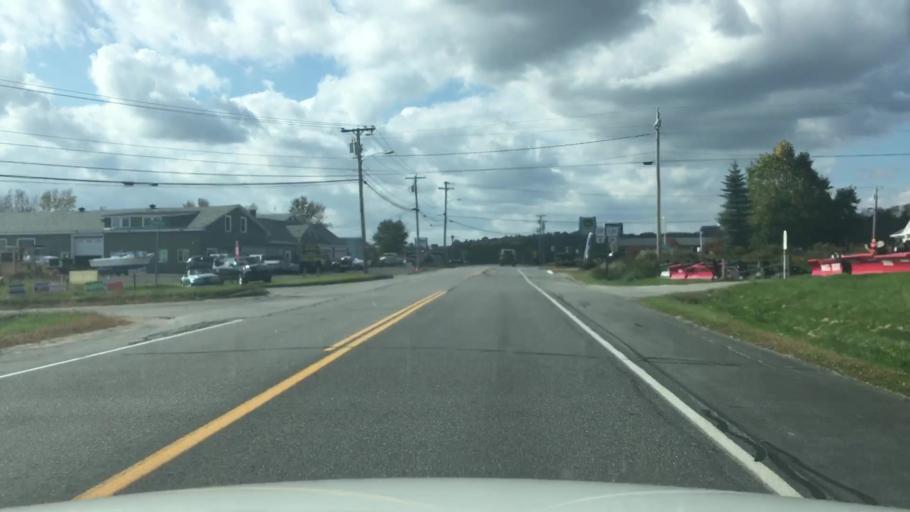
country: US
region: Maine
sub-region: Knox County
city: Union
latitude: 44.2173
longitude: -69.2824
